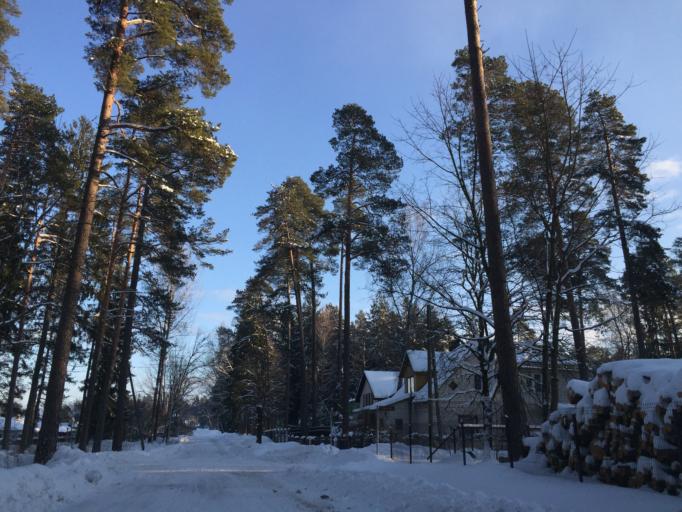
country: LV
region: Incukalns
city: Incukalns
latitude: 57.1024
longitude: 24.6745
